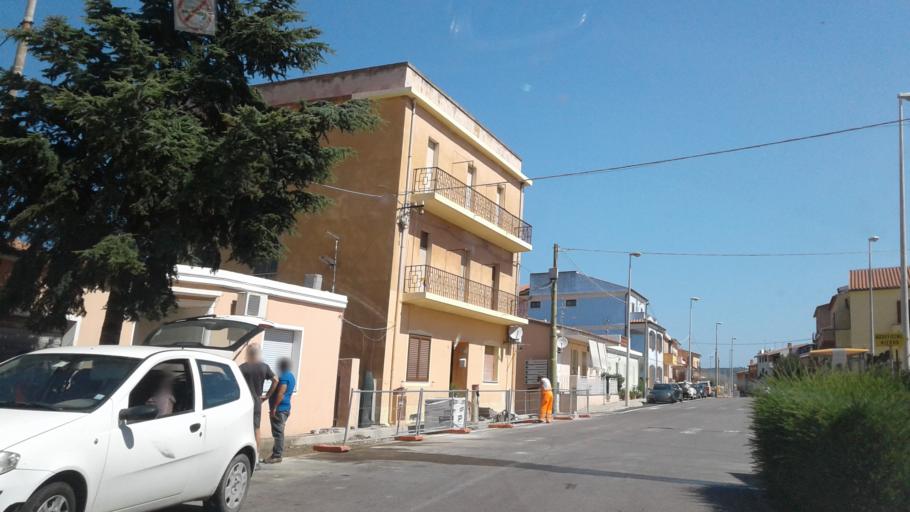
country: IT
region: Sardinia
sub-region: Provincia di Olbia-Tempio
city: Luogosanto
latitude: 41.1085
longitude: 9.2613
